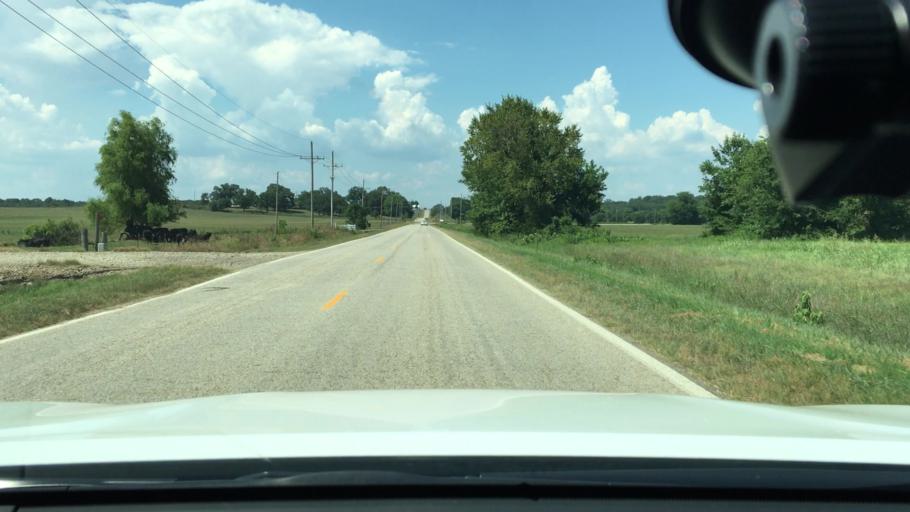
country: US
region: Arkansas
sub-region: Logan County
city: Paris
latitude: 35.3323
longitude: -93.6319
